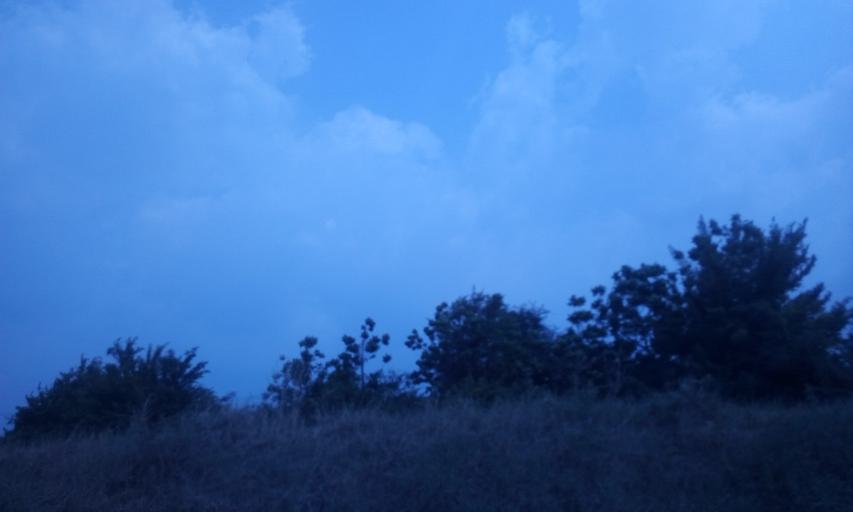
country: TH
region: Chon Buri
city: Ban Bueng
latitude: 13.3401
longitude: 101.1909
